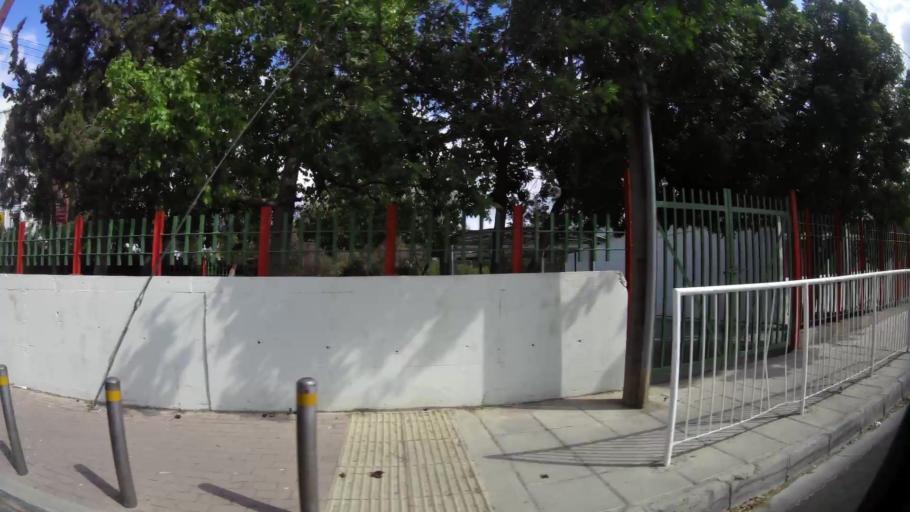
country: CY
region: Lefkosia
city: Nicosia
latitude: 35.1871
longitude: 33.3861
